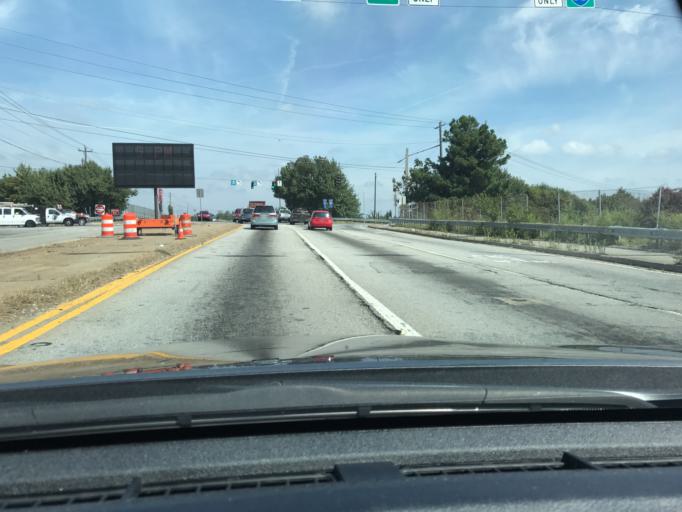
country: US
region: Georgia
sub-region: DeKalb County
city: Doraville
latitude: 33.8998
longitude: -84.2436
